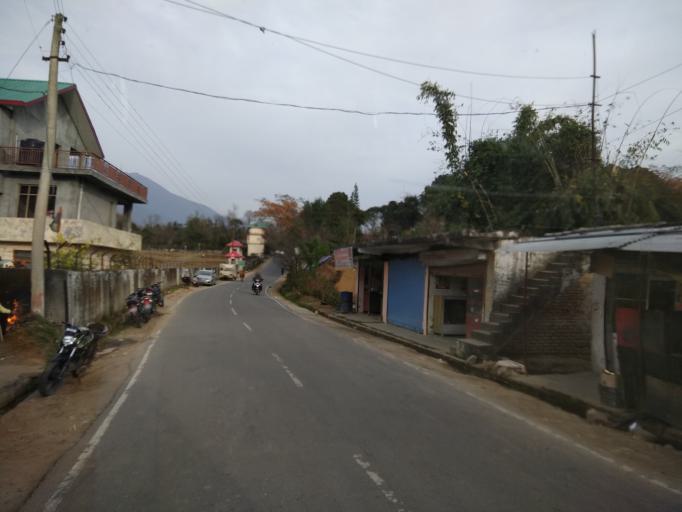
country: IN
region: Himachal Pradesh
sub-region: Kangra
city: Palampur
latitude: 32.1141
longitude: 76.5188
